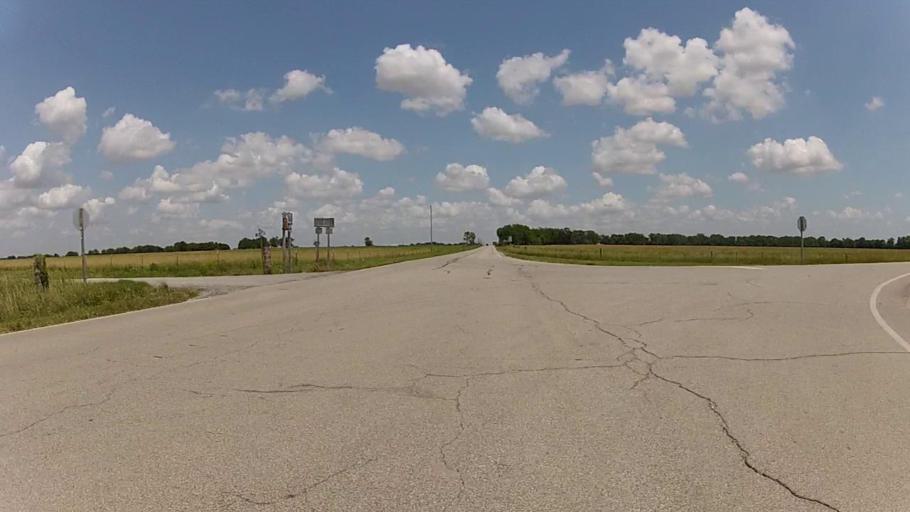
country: US
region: Kansas
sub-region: Labette County
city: Altamont
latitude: 37.1925
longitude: -95.3585
